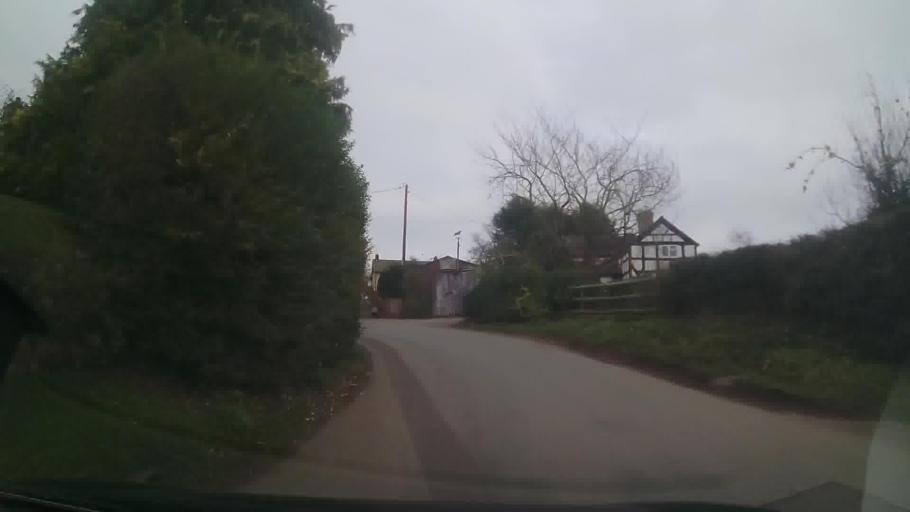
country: GB
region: England
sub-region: Shropshire
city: Bicton
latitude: 52.7681
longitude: -2.8406
